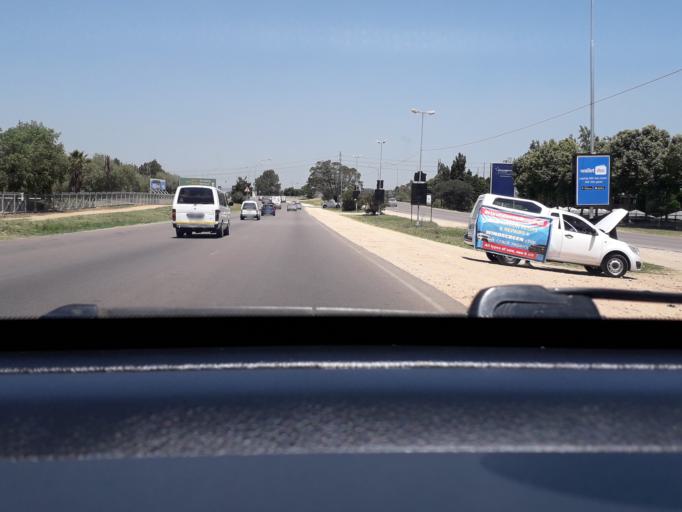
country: ZA
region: Gauteng
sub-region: City of Johannesburg Metropolitan Municipality
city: Midrand
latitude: -26.0592
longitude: 28.0907
